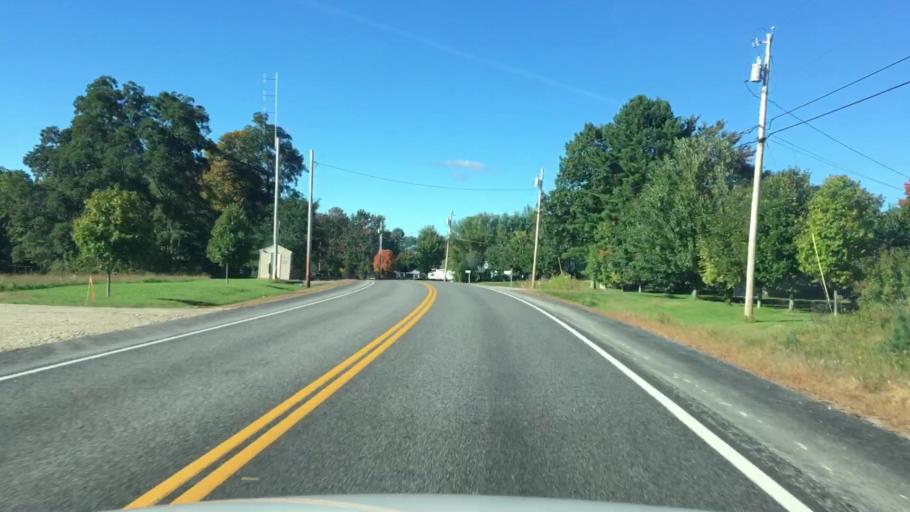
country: US
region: Maine
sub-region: Androscoggin County
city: Lisbon Falls
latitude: 44.0295
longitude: -70.0676
